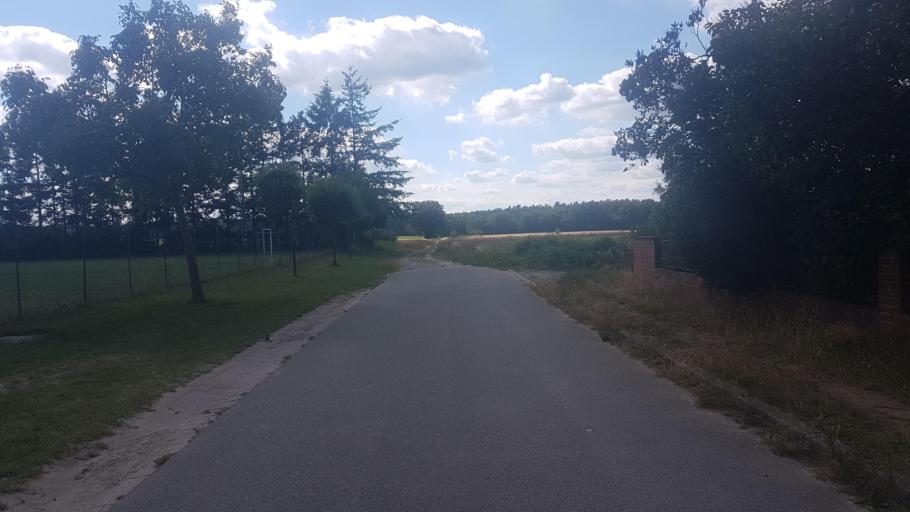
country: DE
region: Lower Saxony
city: Dahlem
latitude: 53.2424
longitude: 10.7725
